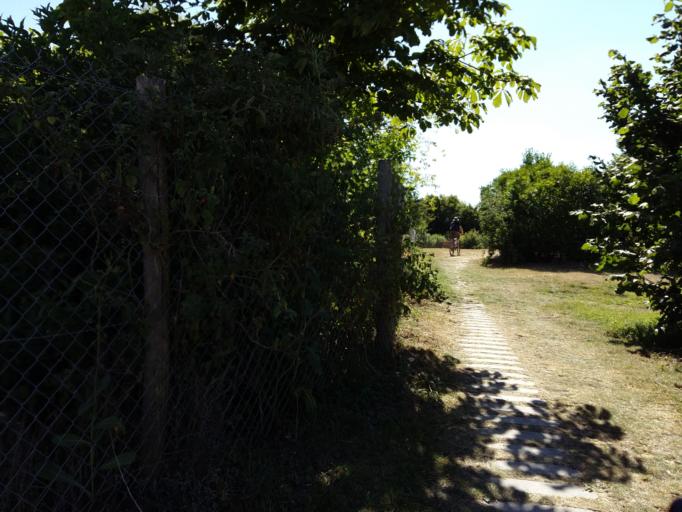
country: FR
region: Picardie
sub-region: Departement de la Somme
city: Dreuil-les-Amiens
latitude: 49.9194
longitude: 2.2625
